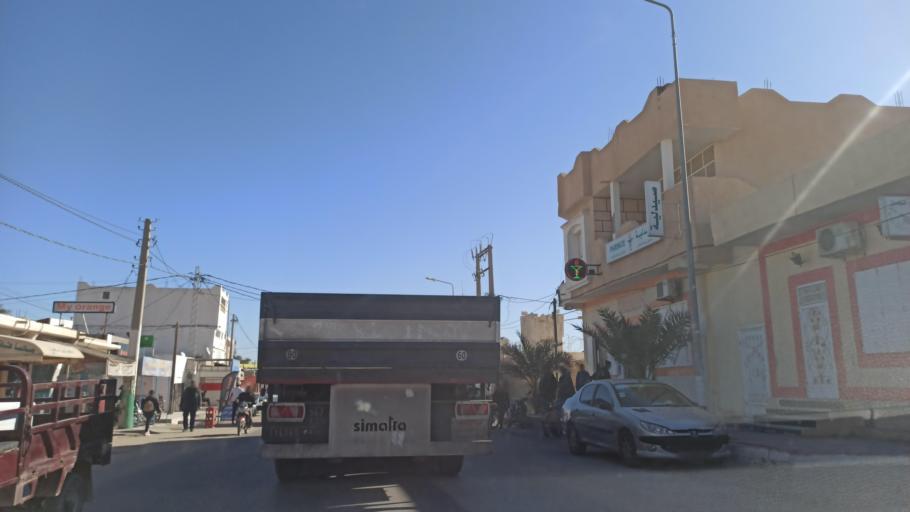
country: TN
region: Gafsa
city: Al Metlaoui
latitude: 34.3159
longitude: 8.4001
